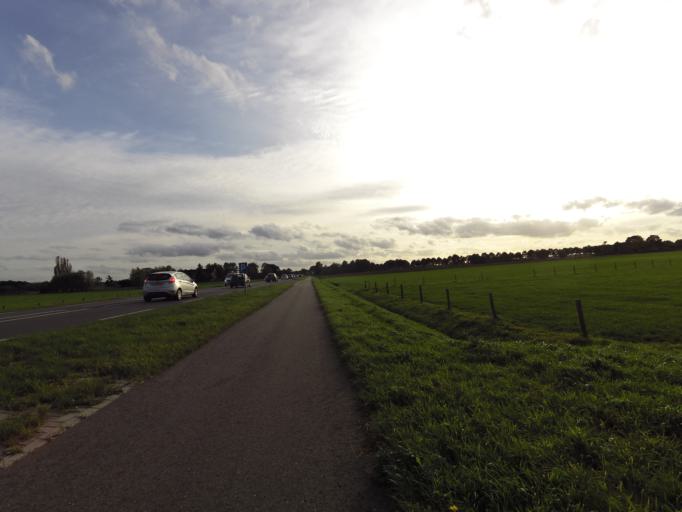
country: NL
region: Gelderland
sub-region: Gemeente Bronckhorst
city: Baak
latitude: 52.0420
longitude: 6.2186
